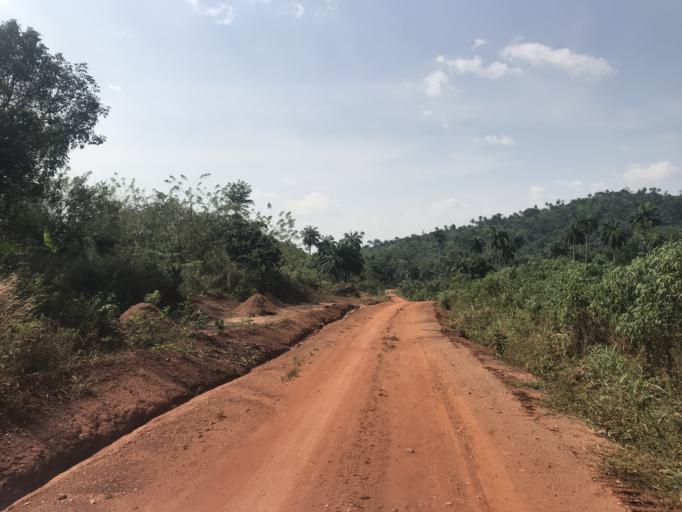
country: NG
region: Osun
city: Ilesa
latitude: 7.6292
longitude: 4.6899
